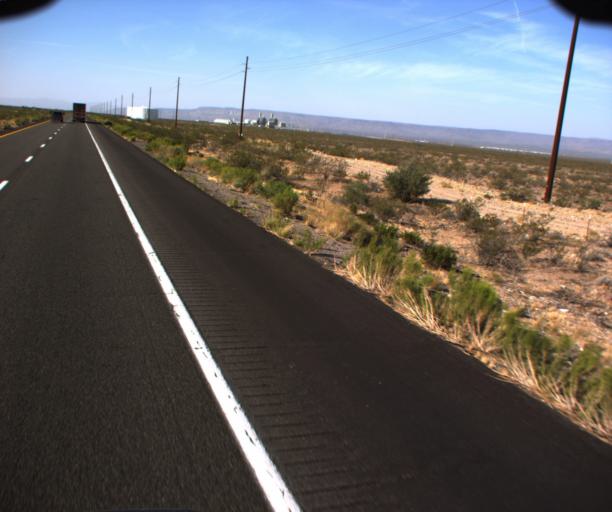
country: US
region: Arizona
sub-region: Mohave County
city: Kingman
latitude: 35.0705
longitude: -114.1239
